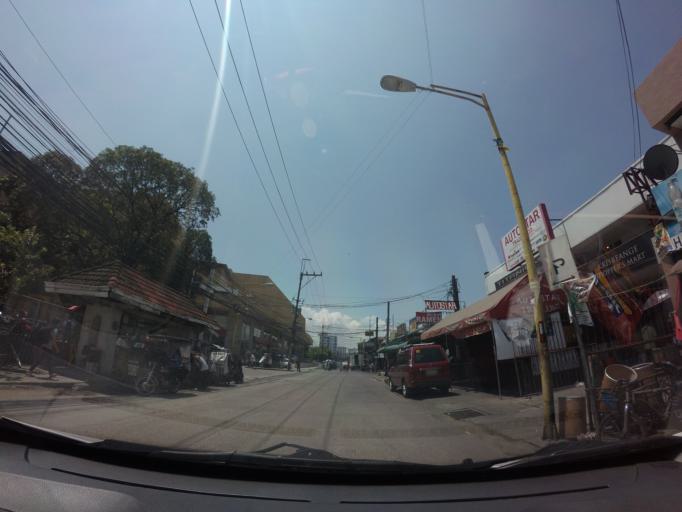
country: PH
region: Metro Manila
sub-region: Makati City
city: Makati City
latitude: 14.5589
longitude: 121.0052
